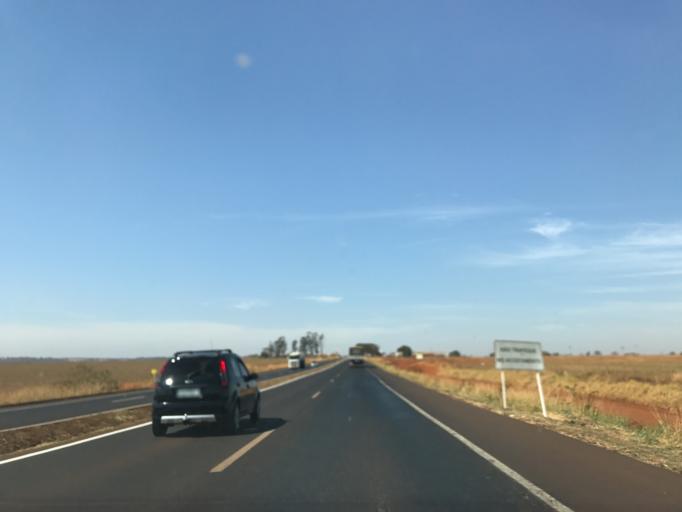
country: BR
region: Minas Gerais
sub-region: Centralina
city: Centralina
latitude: -18.5600
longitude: -49.1939
